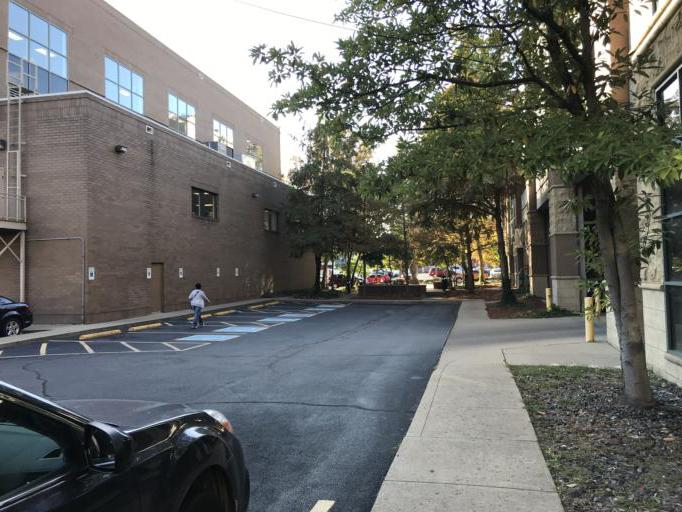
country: US
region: Kentucky
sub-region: Jefferson County
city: Louisville
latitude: 38.2492
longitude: -85.7536
